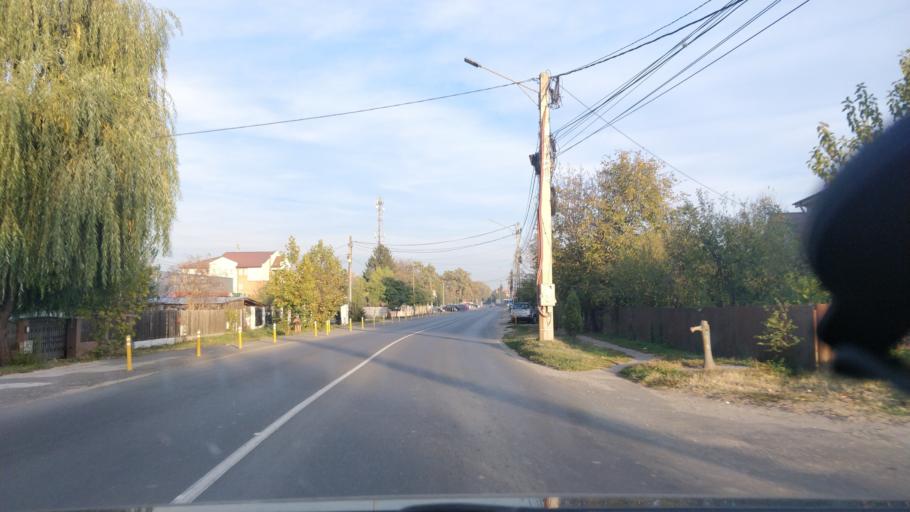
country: RO
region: Ilfov
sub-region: Comuna Ciorogarla
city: Ciorogarla
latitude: 44.4434
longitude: 25.8797
